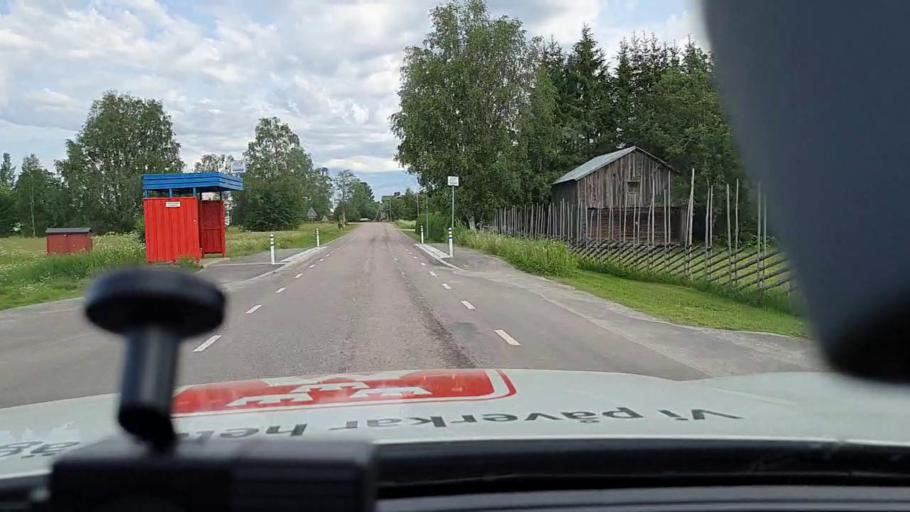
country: SE
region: Norrbotten
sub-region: Bodens Kommun
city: Saevast
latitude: 65.6824
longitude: 21.7998
